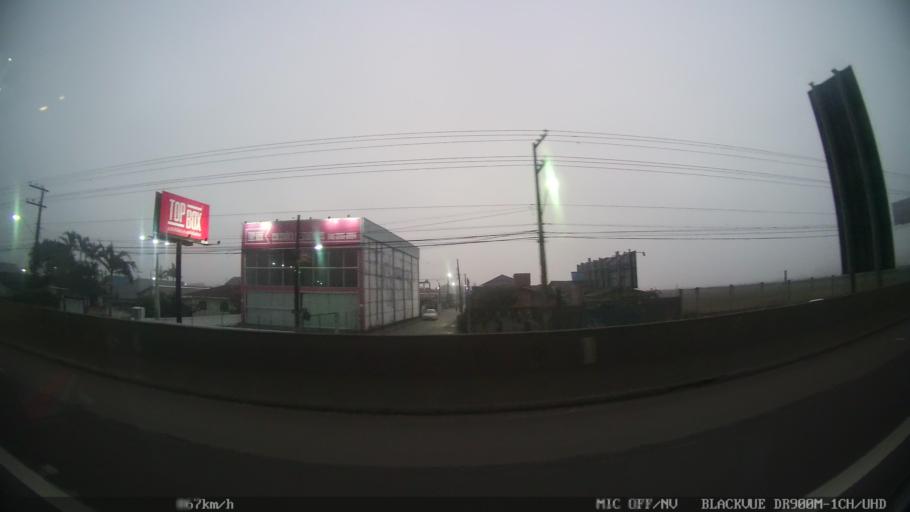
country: BR
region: Santa Catarina
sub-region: Biguacu
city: Biguacu
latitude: -27.5127
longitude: -48.6398
